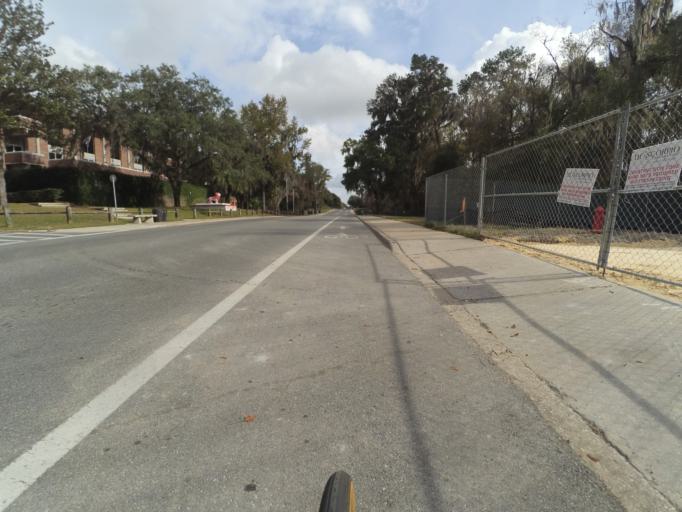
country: US
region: Florida
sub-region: Alachua County
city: Gainesville
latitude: 29.6448
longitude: -82.3557
